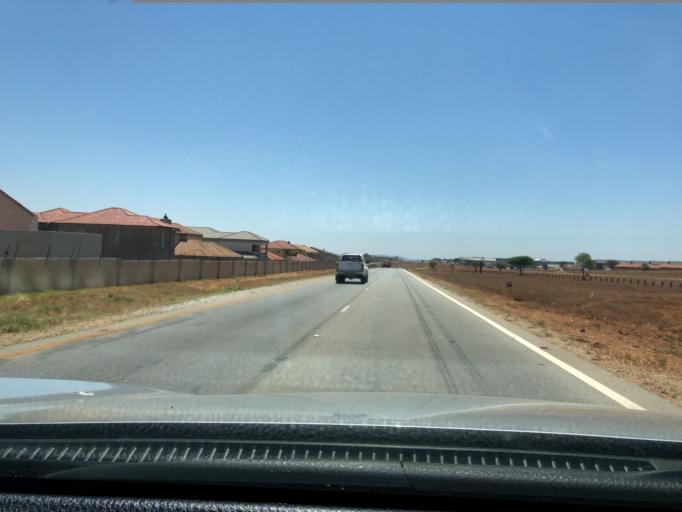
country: ZA
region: Limpopo
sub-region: Capricorn District Municipality
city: Polokwane
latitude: -23.8848
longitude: 29.5076
